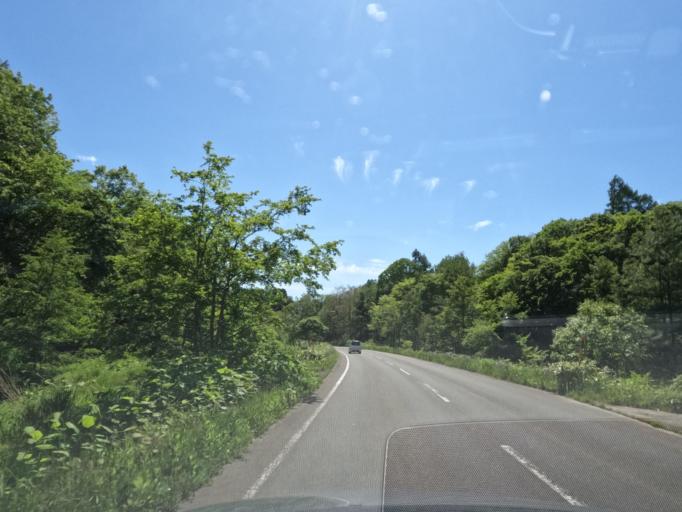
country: JP
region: Hokkaido
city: Iwamizawa
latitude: 43.1039
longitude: 141.7853
